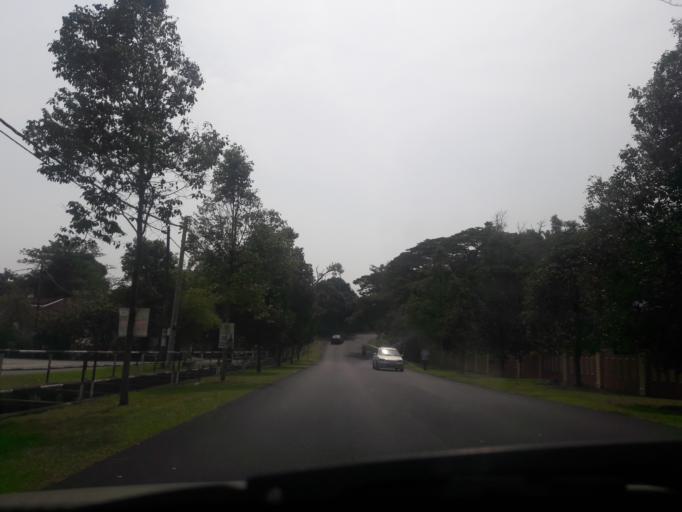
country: MY
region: Kedah
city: Kulim
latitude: 5.3692
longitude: 100.5625
